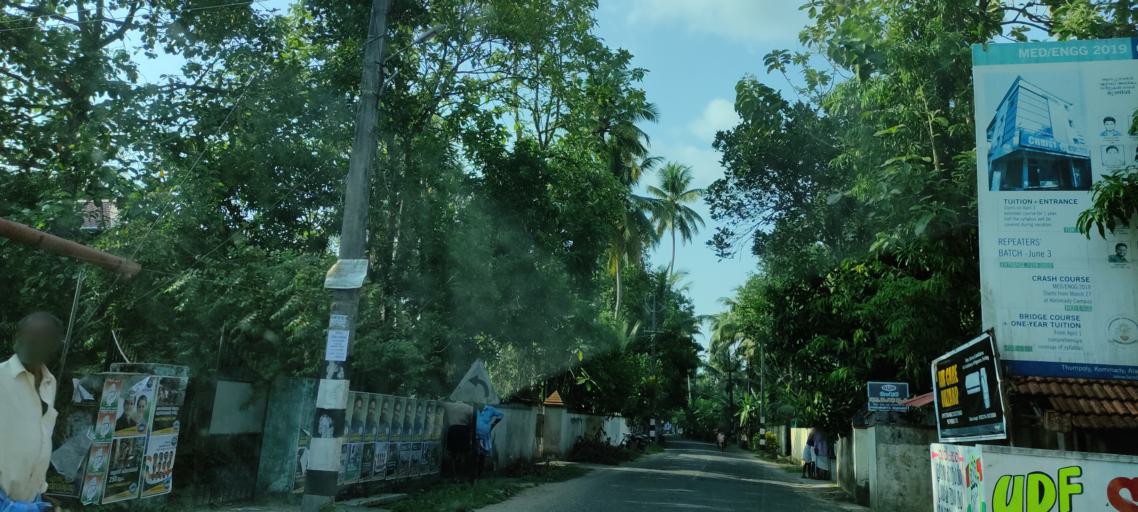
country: IN
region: Kerala
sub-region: Alappuzha
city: Vayalar
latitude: 9.7012
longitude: 76.2896
